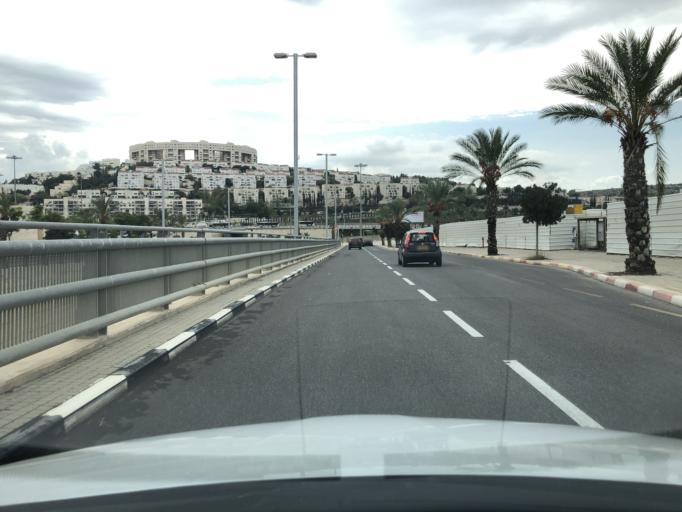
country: IL
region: Central District
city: Modiin
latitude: 31.9016
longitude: 35.0050
